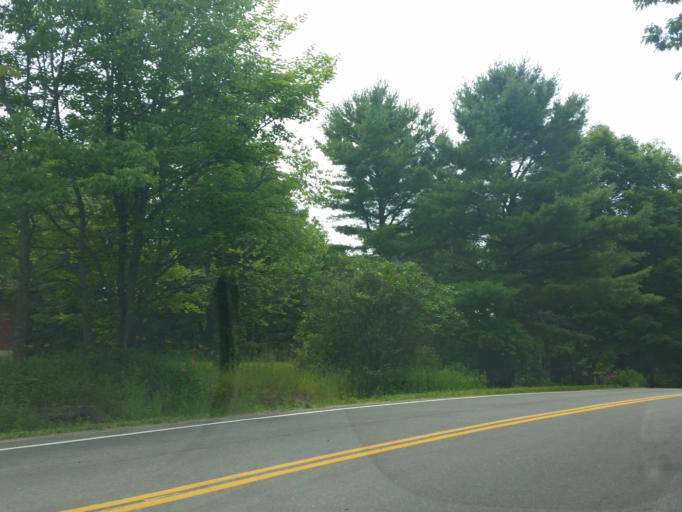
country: CA
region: Ontario
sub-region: Parry Sound District
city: Parry Sound
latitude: 45.3951
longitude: -80.0275
